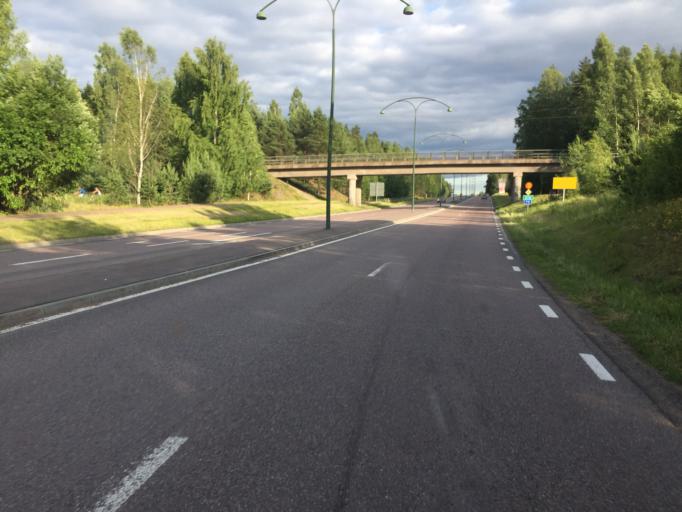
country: SE
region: Dalarna
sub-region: Borlange Kommun
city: Borlaenge
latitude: 60.5054
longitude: 15.3876
